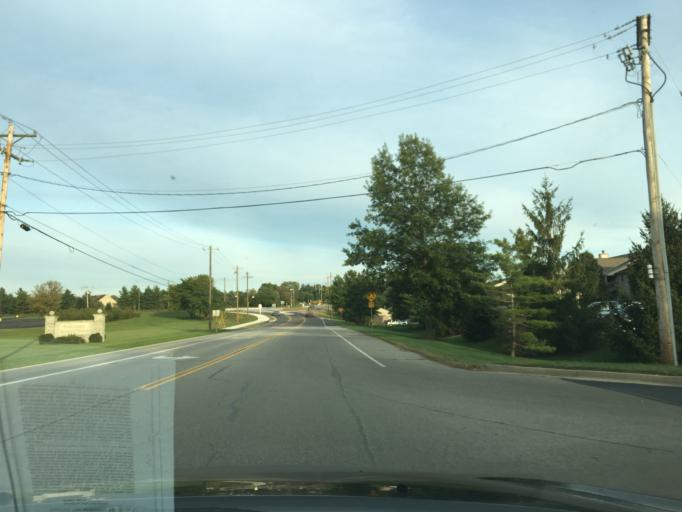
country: US
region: Ohio
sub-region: Butler County
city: Beckett Ridge
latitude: 39.3511
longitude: -84.4556
